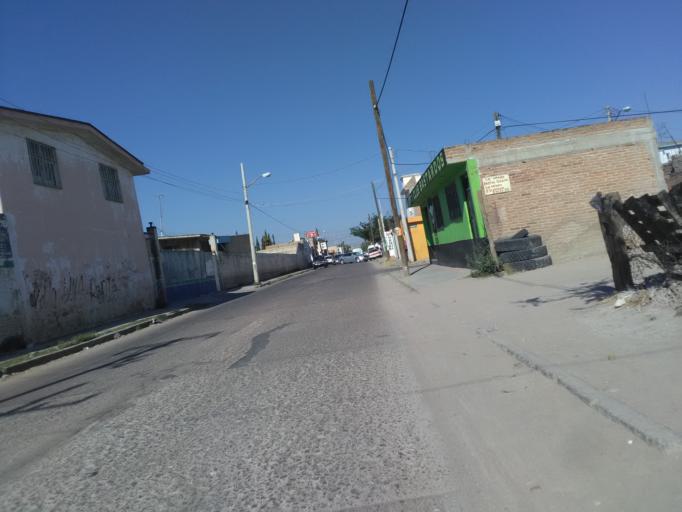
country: MX
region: Durango
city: Victoria de Durango
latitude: 24.0134
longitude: -104.6409
